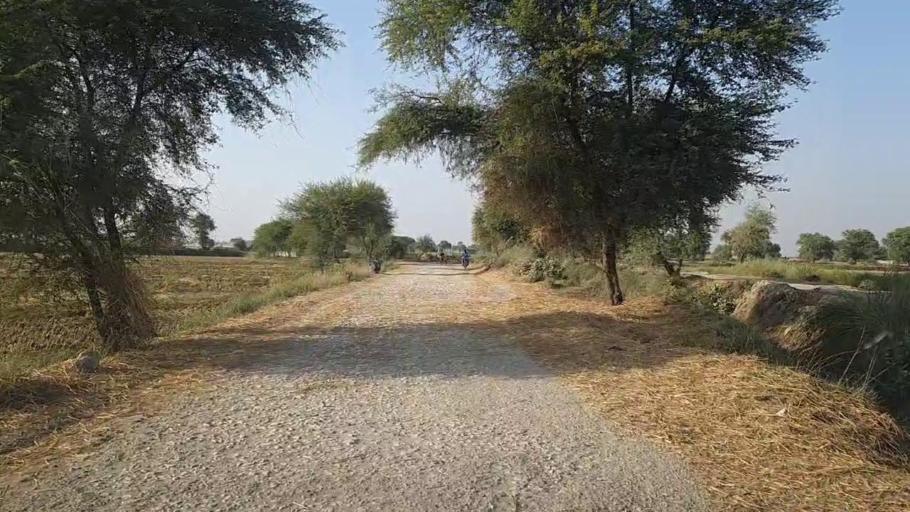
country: PK
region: Sindh
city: Kashmor
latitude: 28.4062
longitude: 69.4141
